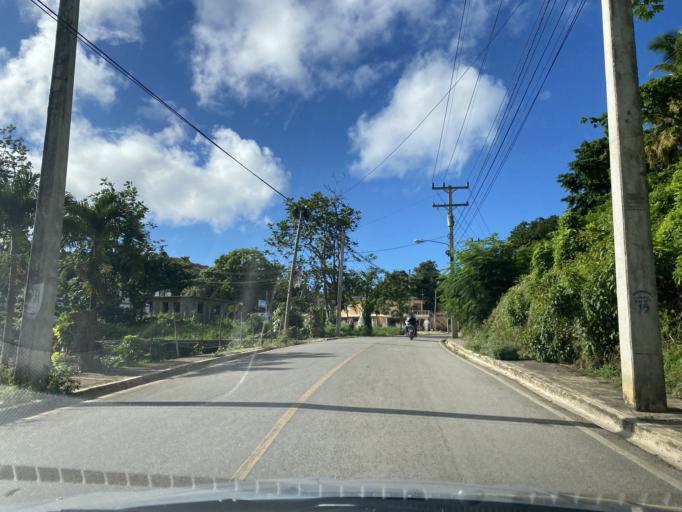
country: DO
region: Samana
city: Las Terrenas
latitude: 19.2950
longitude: -69.5492
